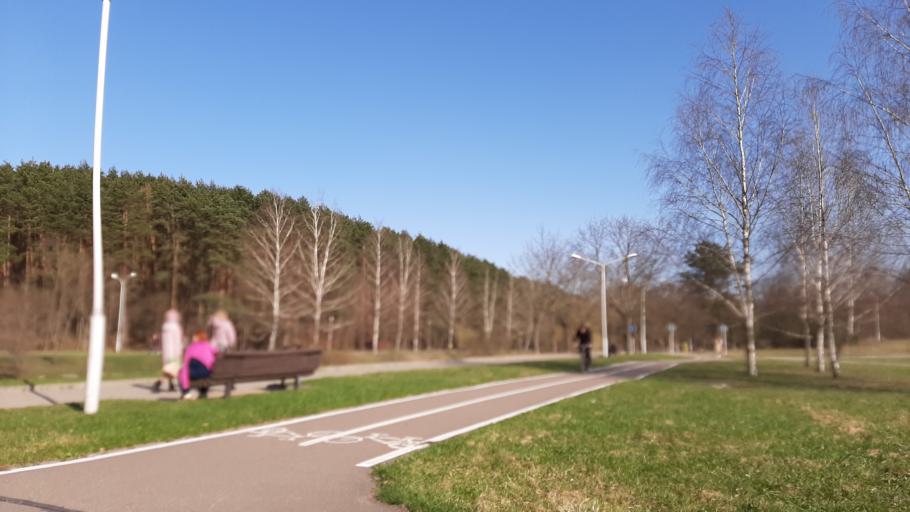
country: BY
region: Minsk
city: Bal'shavik
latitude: 53.9600
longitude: 27.5941
